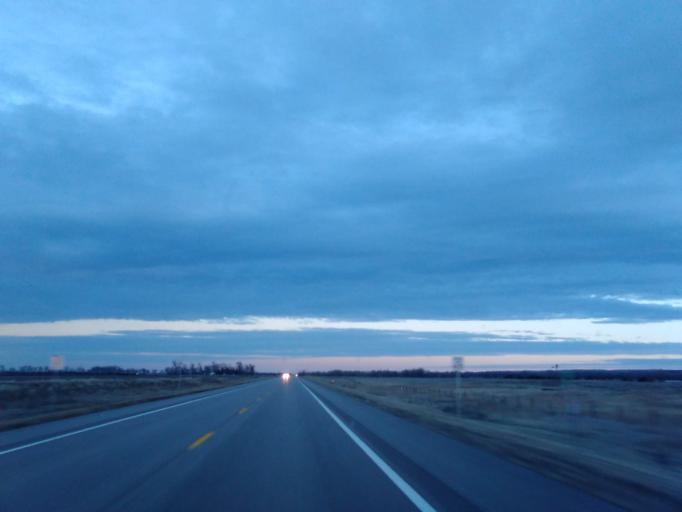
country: US
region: Nebraska
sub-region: Garden County
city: Oshkosh
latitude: 41.3695
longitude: -102.2413
